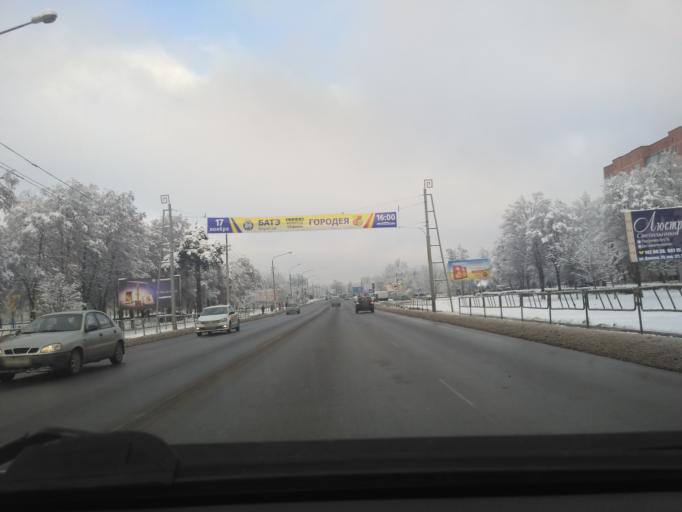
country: BY
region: Minsk
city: Horad Barysaw
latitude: 54.2218
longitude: 28.4927
